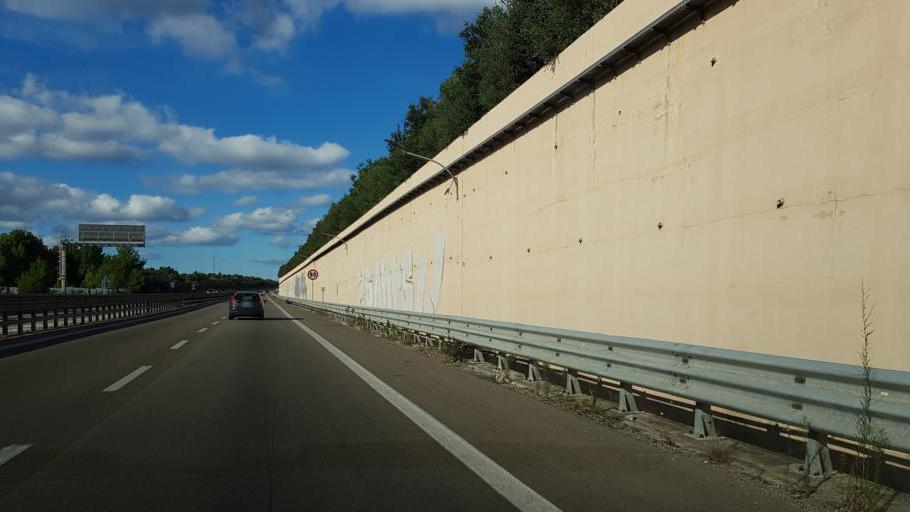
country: IT
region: Apulia
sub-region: Provincia di Lecce
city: Arnesano
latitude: 40.3437
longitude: 18.1251
